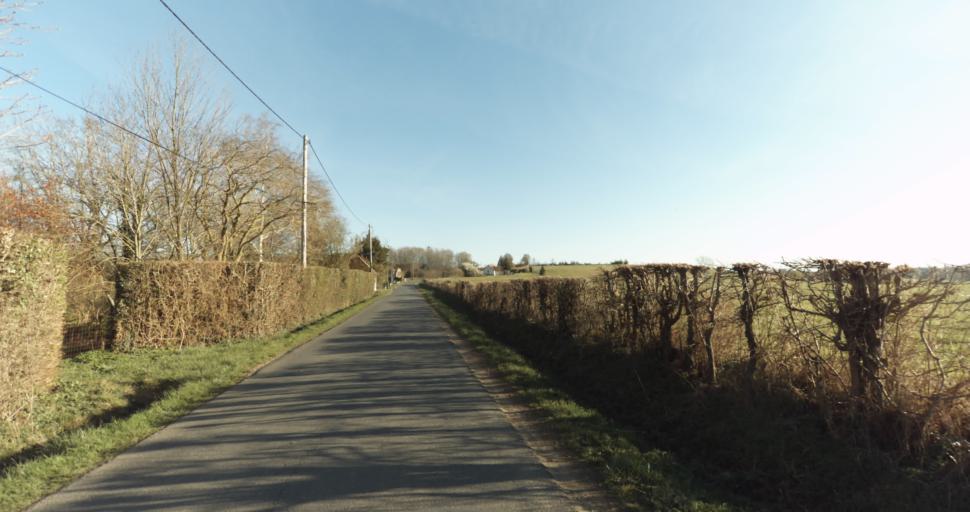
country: FR
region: Lower Normandy
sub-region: Departement de l'Orne
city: Trun
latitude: 48.9151
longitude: 0.0325
